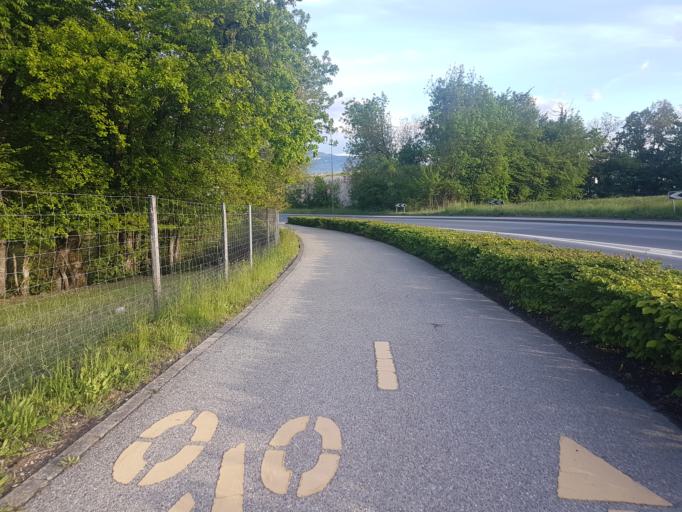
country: CH
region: Geneva
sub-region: Geneva
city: Aire-la-Ville
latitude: 46.2030
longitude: 6.0631
